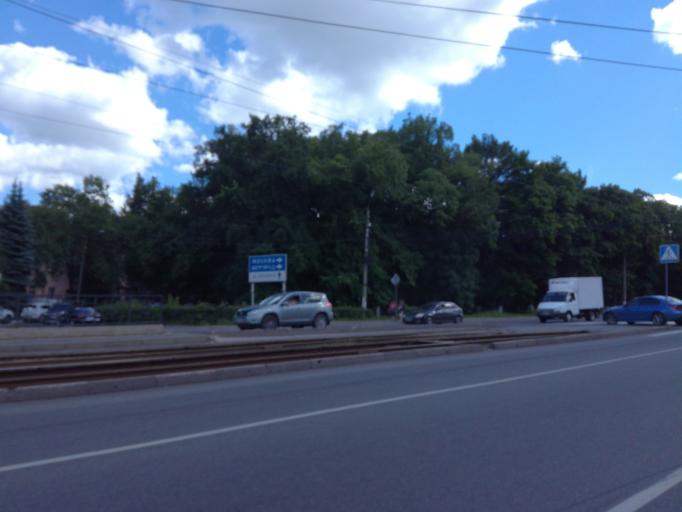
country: RU
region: Kursk
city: Kursk
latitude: 51.7510
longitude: 36.1993
